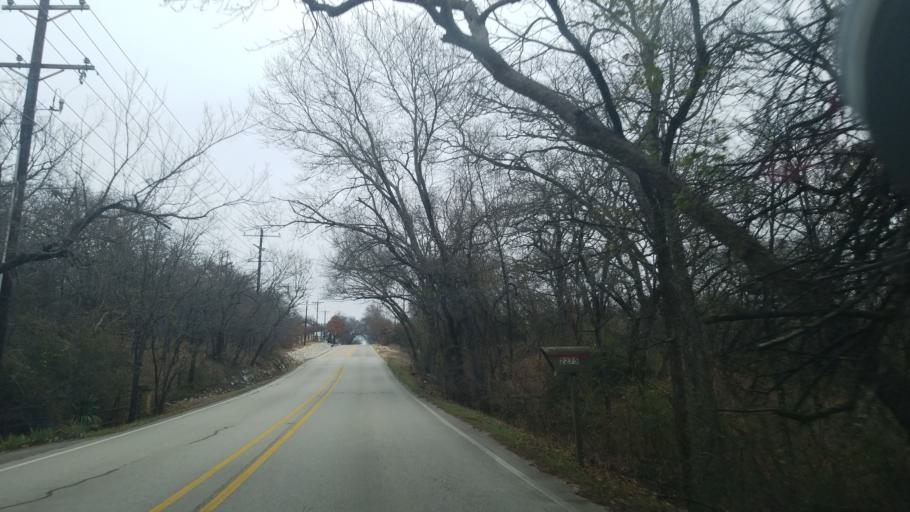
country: US
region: Texas
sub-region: Denton County
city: Copper Canyon
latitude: 33.1178
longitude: -97.1169
